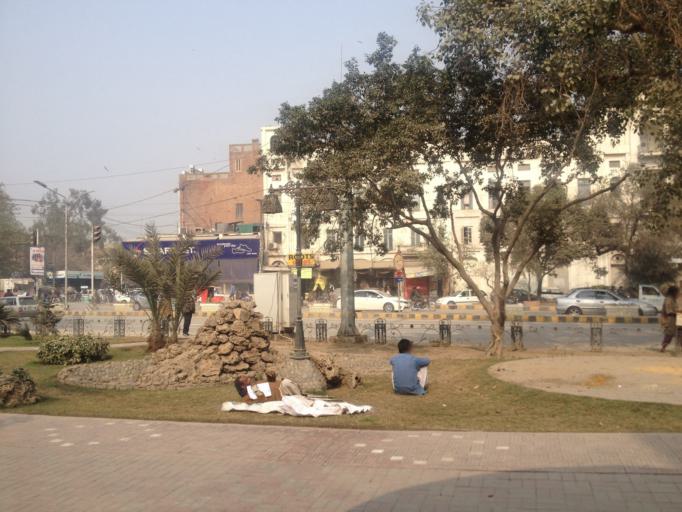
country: PK
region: Punjab
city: Lahore
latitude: 31.5676
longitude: 74.3103
